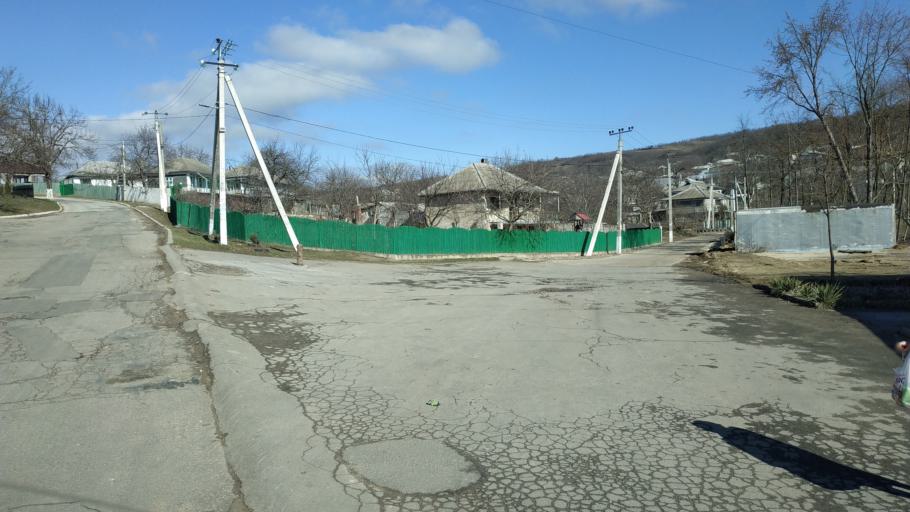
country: MD
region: Straseni
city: Straseni
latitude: 47.0179
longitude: 28.5449
